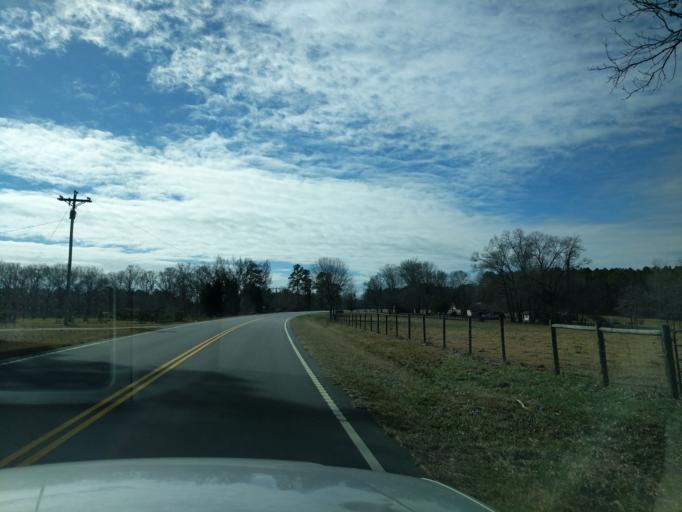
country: US
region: South Carolina
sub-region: Saluda County
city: Saluda
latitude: 33.9557
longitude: -81.9016
